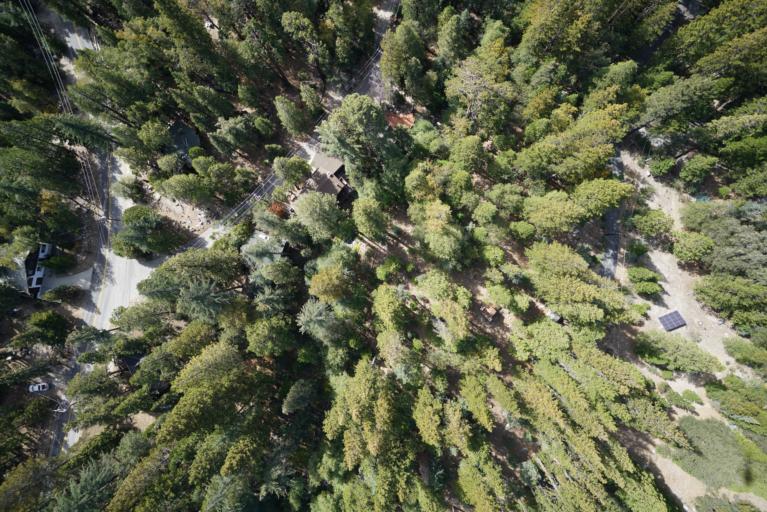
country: US
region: California
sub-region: Riverside County
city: Idyllwild
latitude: 33.7642
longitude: -116.6941
